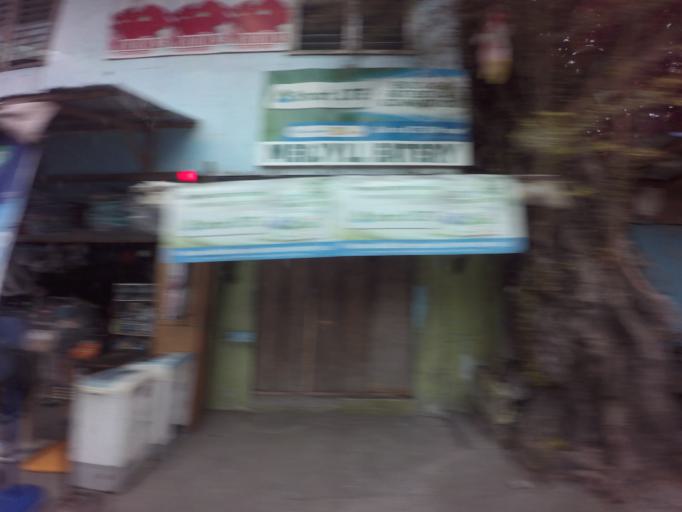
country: PH
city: Sambayanihan People's Village
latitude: 14.4661
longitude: 121.0560
